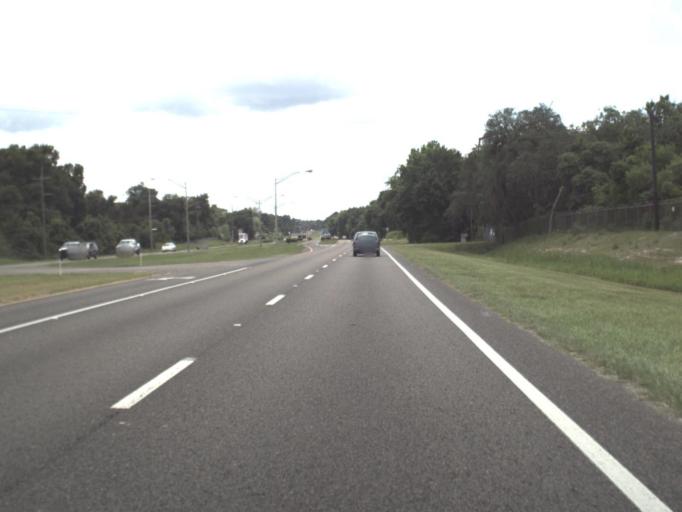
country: US
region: Florida
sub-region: Putnam County
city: East Palatka
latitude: 29.6271
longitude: -81.5873
